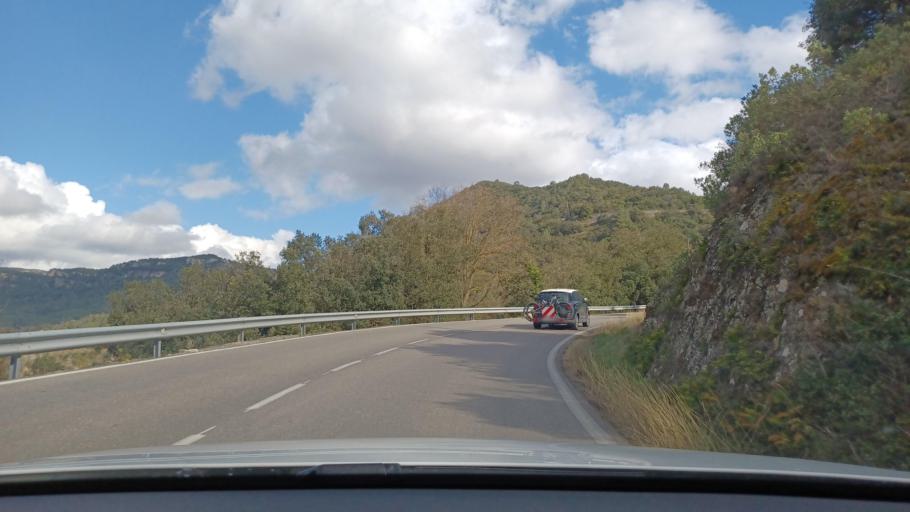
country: ES
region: Catalonia
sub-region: Provincia de Tarragona
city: la Morera de Montsant
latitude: 41.2294
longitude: 0.9043
